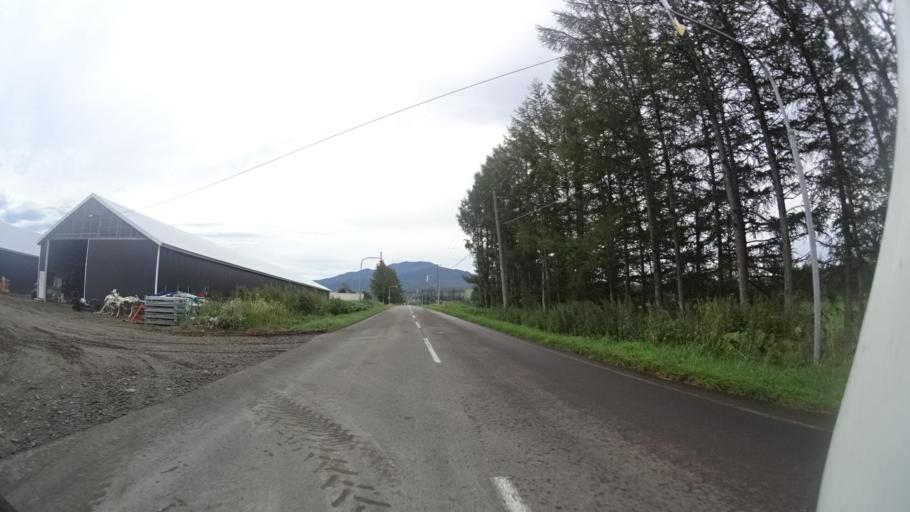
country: JP
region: Hokkaido
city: Shibetsu
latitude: 43.8737
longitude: 144.7303
